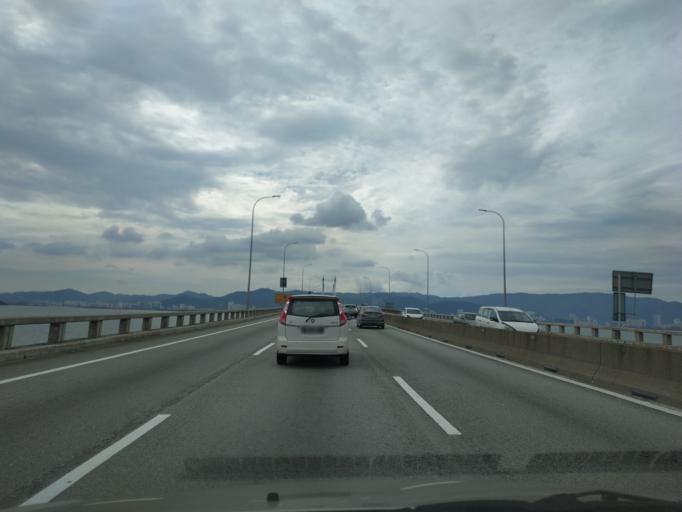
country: MY
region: Penang
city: Perai
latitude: 5.3523
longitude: 100.3572
